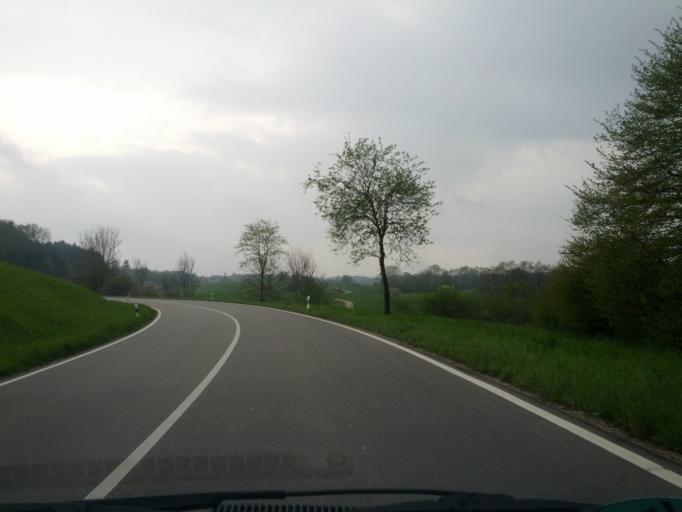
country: DE
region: Baden-Wuerttemberg
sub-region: Freiburg Region
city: Hasel
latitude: 47.6493
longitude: 7.8866
